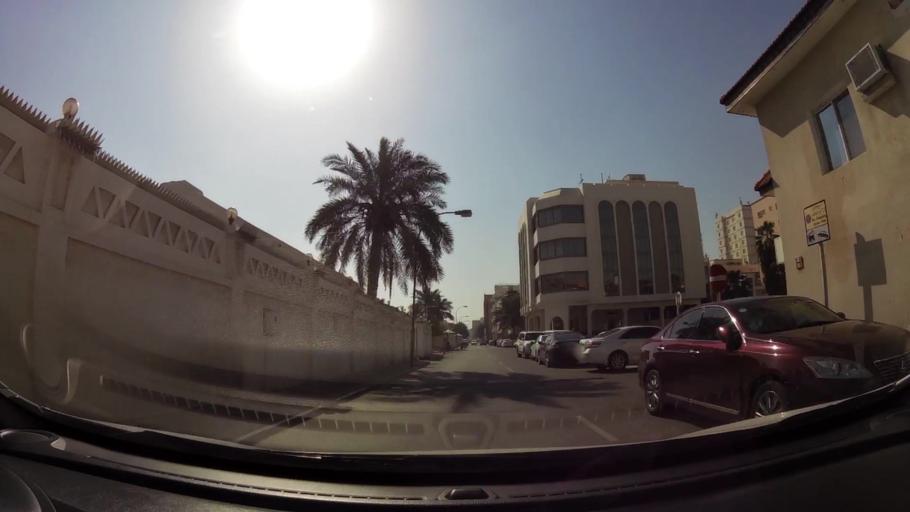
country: BH
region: Manama
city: Manama
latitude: 26.2135
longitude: 50.5875
